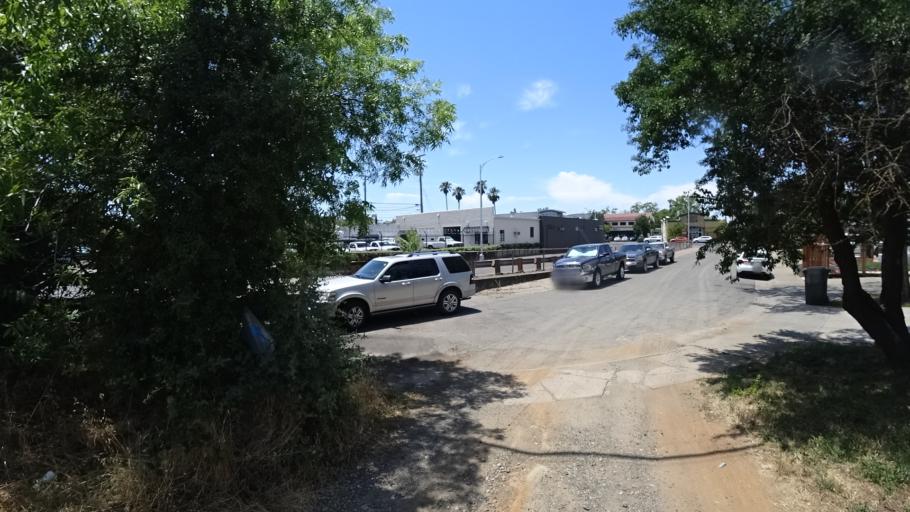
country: US
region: California
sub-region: Sacramento County
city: Sacramento
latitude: 38.5683
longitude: -121.4327
